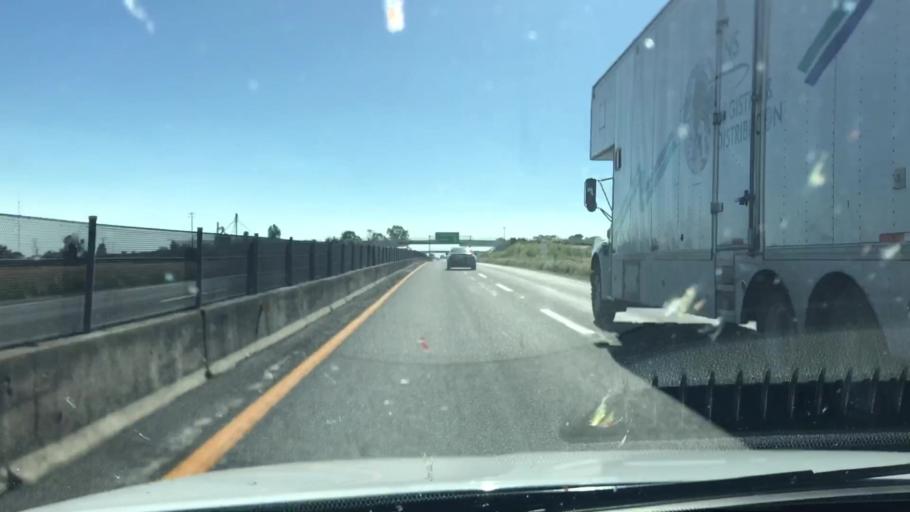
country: MX
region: Jalisco
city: Tepatitlan de Morelos
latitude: 20.8944
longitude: -102.7084
